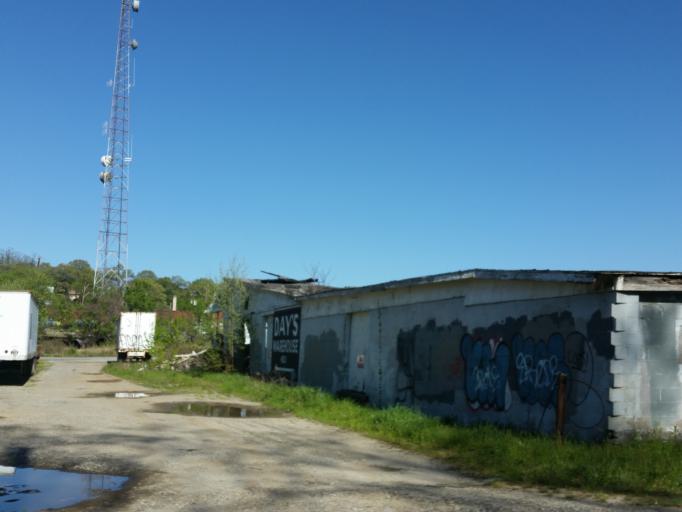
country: US
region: North Carolina
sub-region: Buncombe County
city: Asheville
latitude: 35.5798
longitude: -82.5675
